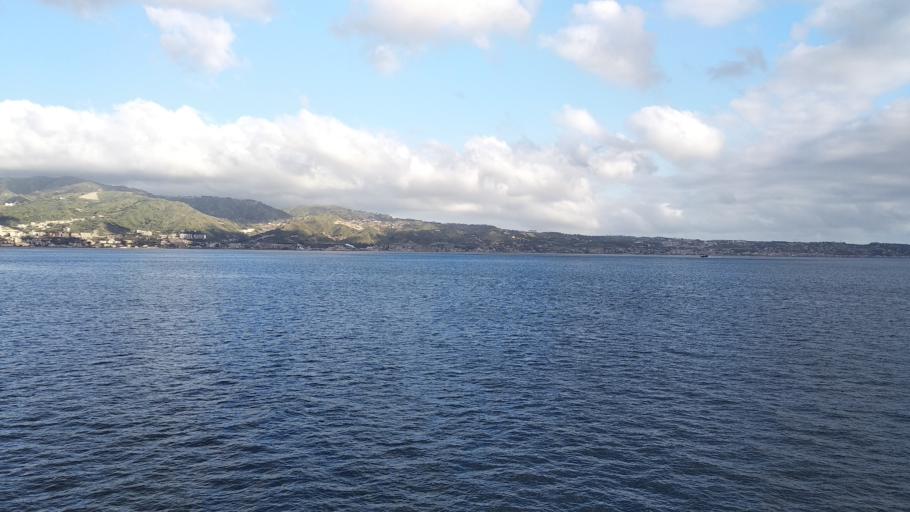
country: IT
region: Calabria
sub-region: Provincia di Reggio Calabria
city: Campo Calabro
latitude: 38.2114
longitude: 15.6113
